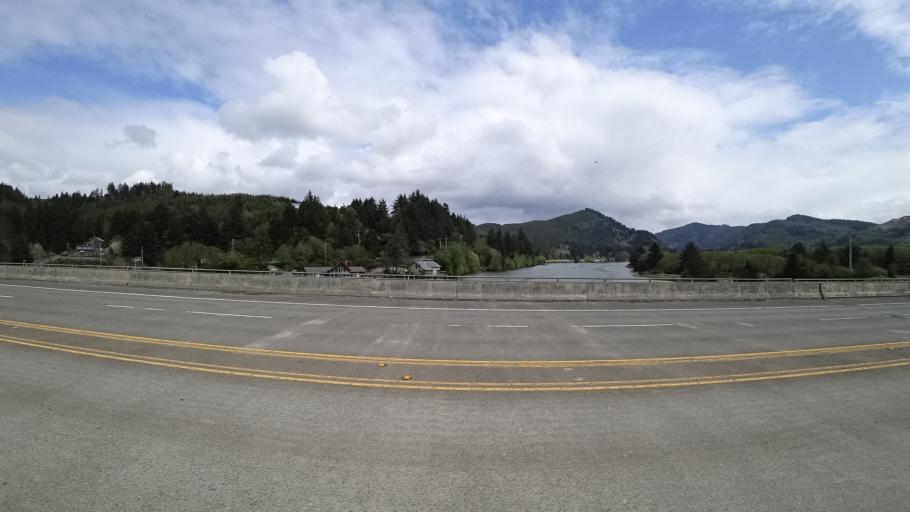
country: US
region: Oregon
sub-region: Lincoln County
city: Lincoln City
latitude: 44.8991
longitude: -124.0079
